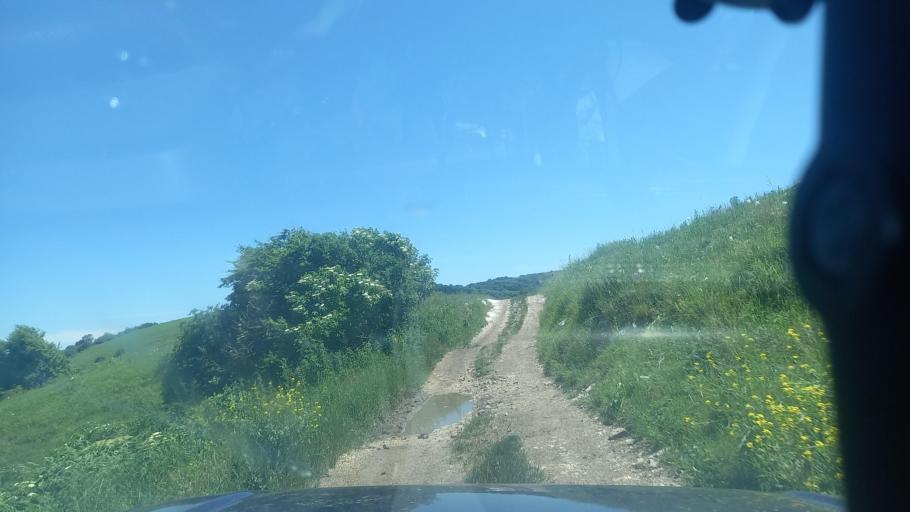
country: RU
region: Karachayevo-Cherkesiya
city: Pregradnaya
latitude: 44.1035
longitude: 41.1230
